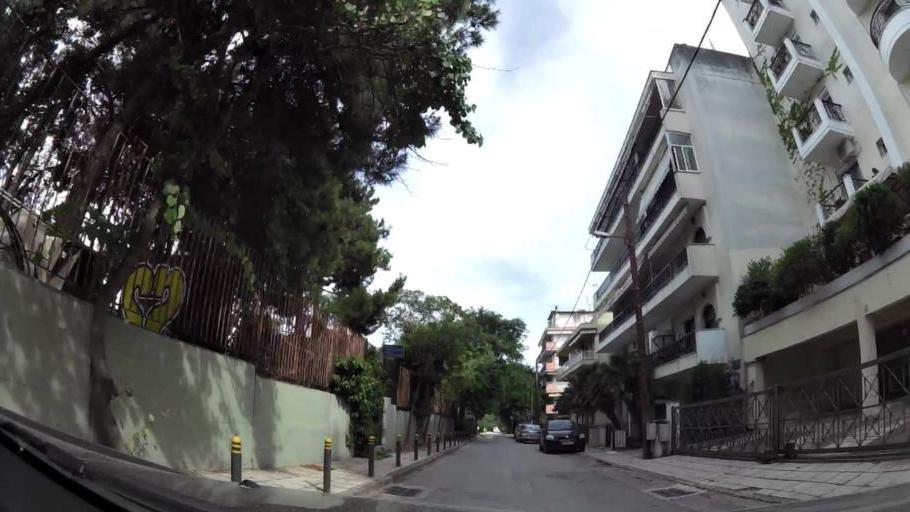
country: GR
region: Central Macedonia
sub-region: Nomos Thessalonikis
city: Kalamaria
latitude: 40.5783
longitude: 22.9522
